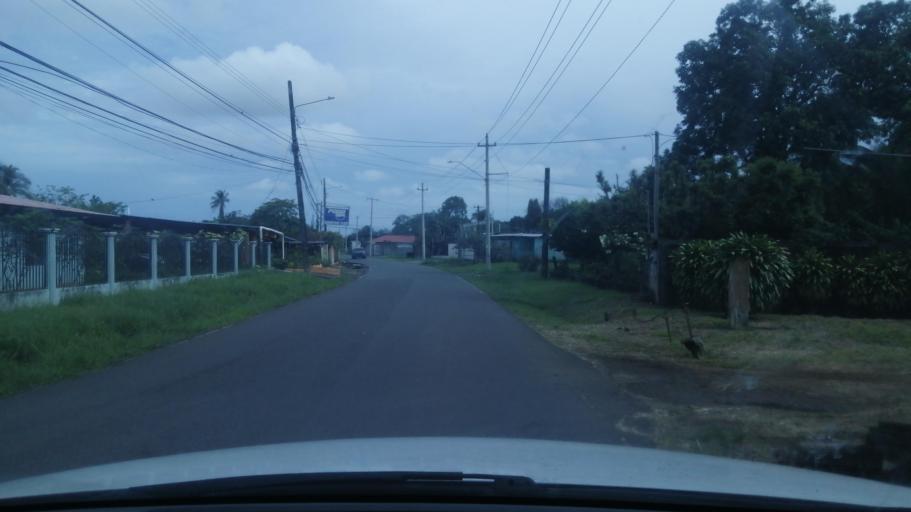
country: PA
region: Chiriqui
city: David
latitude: 8.4106
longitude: -82.4269
